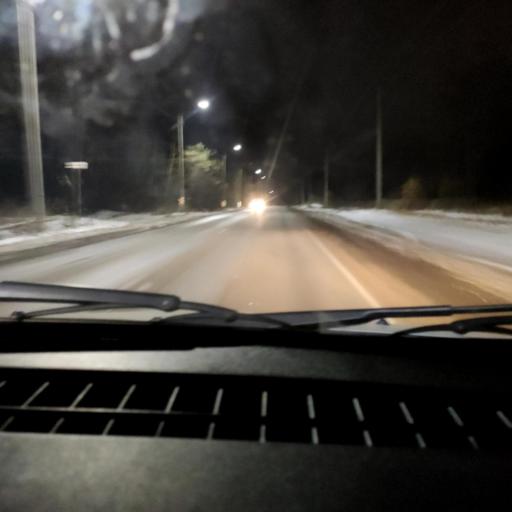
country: RU
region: Voronezj
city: Podgornoye
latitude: 51.7862
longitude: 39.1740
